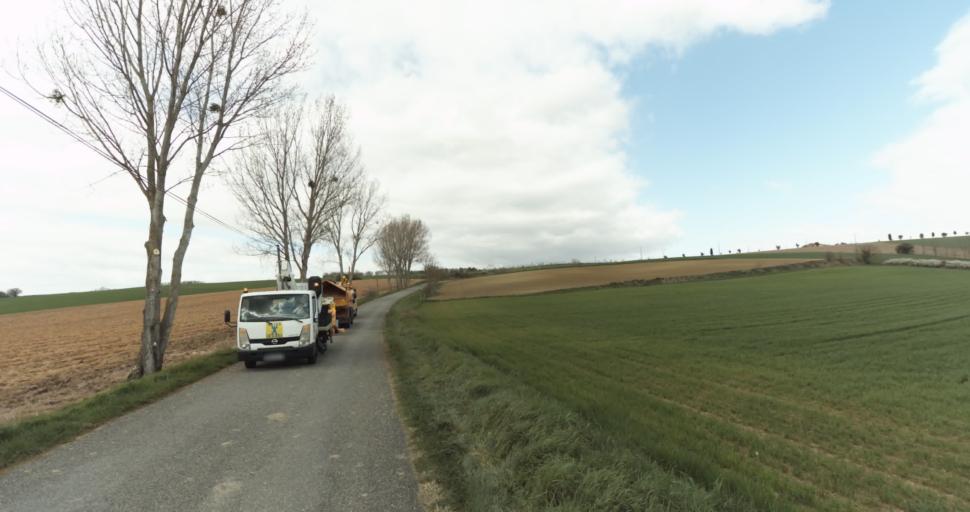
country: FR
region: Midi-Pyrenees
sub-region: Departement de la Haute-Garonne
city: Auterive
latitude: 43.3774
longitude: 1.4845
